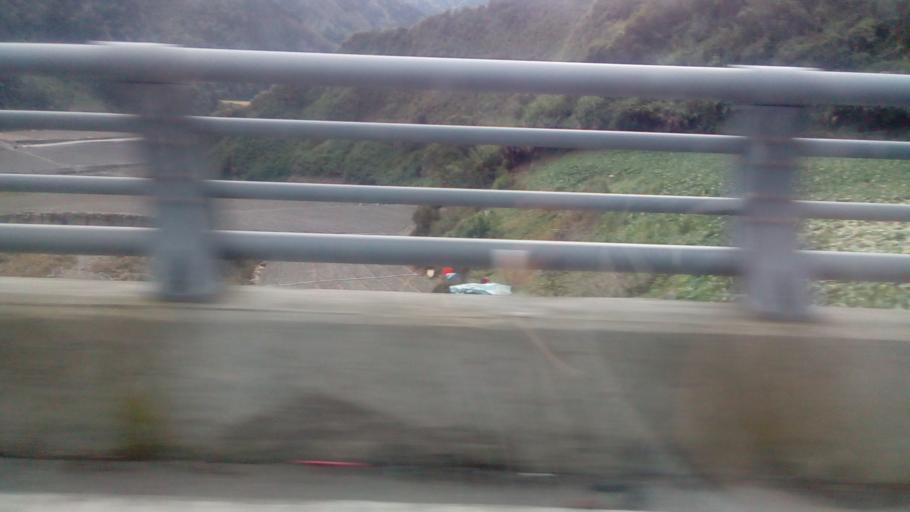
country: TW
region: Taiwan
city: Daxi
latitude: 24.4635
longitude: 121.3949
